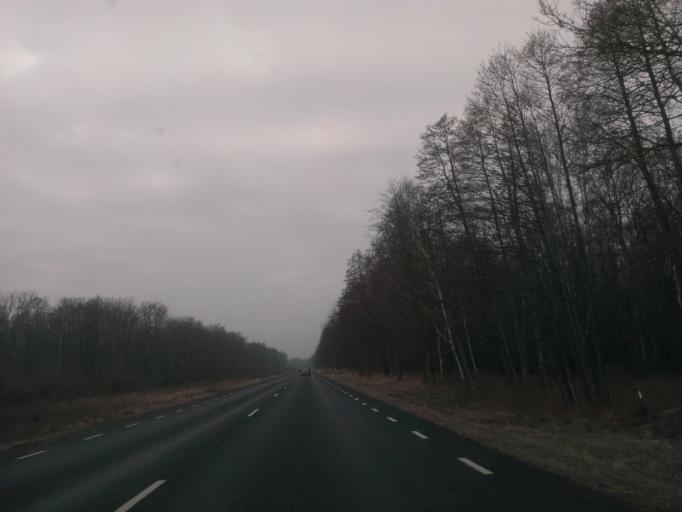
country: EE
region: Saare
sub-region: Orissaare vald
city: Orissaare
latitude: 58.6029
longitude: 23.3080
